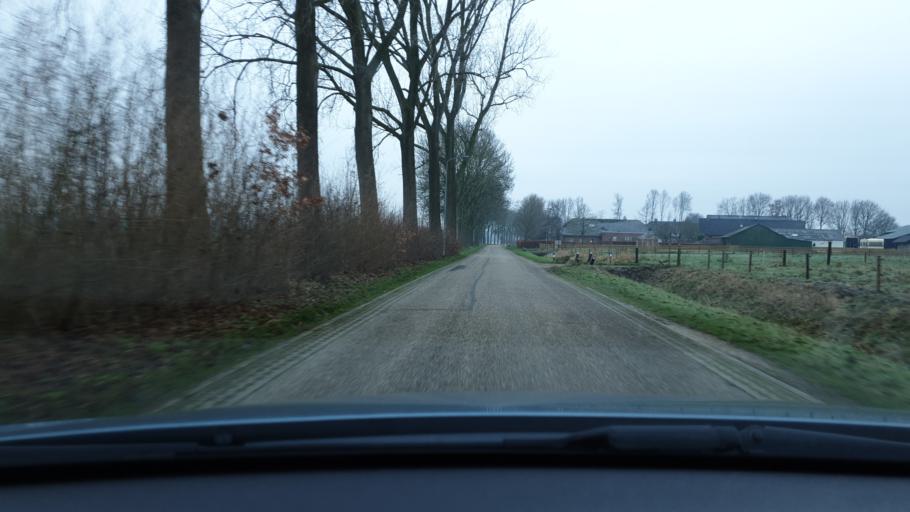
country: NL
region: Gelderland
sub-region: Gemeente Wijchen
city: Bergharen
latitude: 51.8525
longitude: 5.6786
